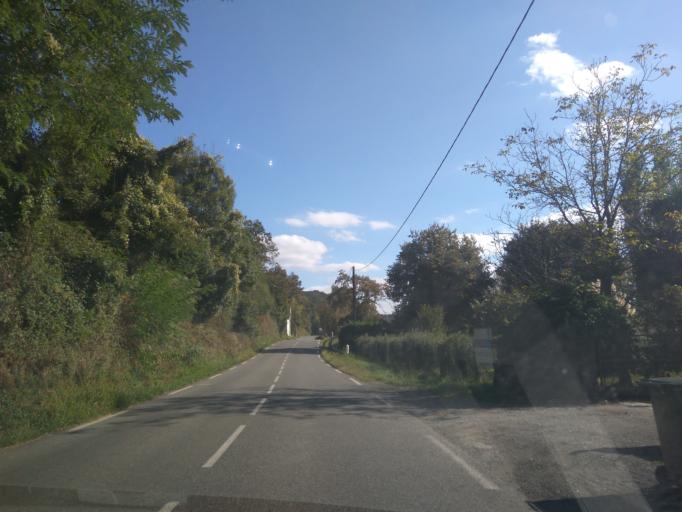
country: FR
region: Aquitaine
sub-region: Departement des Pyrenees-Atlantiques
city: Gelos
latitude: 43.2712
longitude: -0.3700
